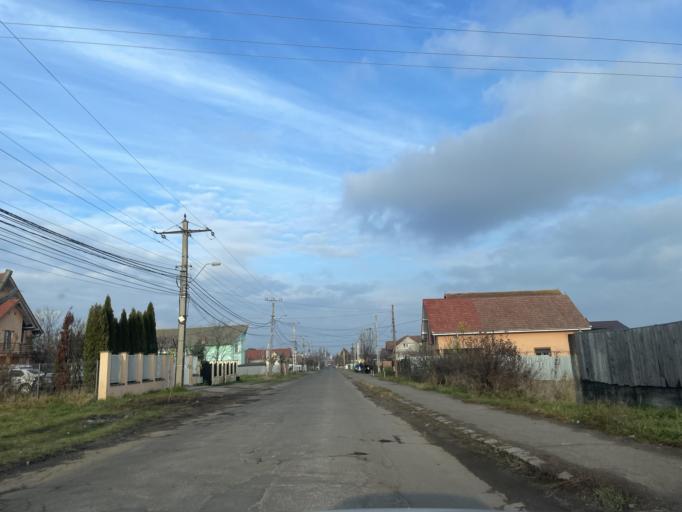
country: RO
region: Mures
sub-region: Municipiul Reghin
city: Apalina
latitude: 46.7636
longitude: 24.6929
